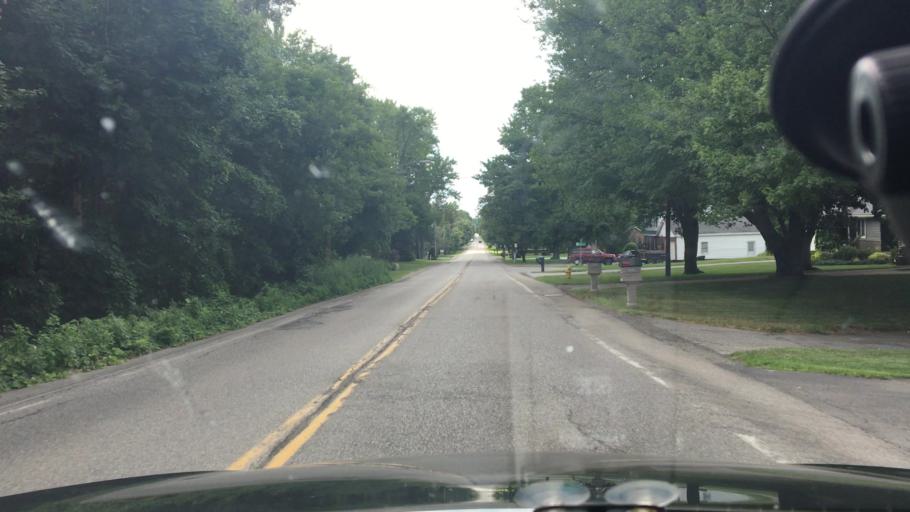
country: US
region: New York
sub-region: Erie County
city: Orchard Park
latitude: 42.7708
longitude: -78.7484
